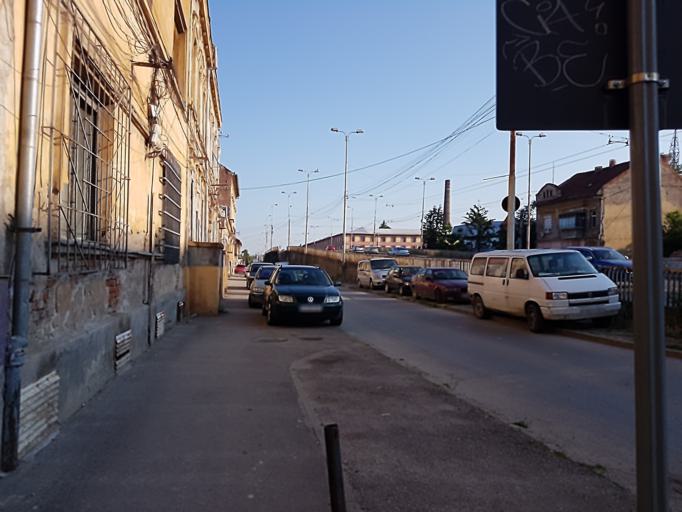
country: RO
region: Timis
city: Timisoara
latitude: 45.7442
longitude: 21.2059
